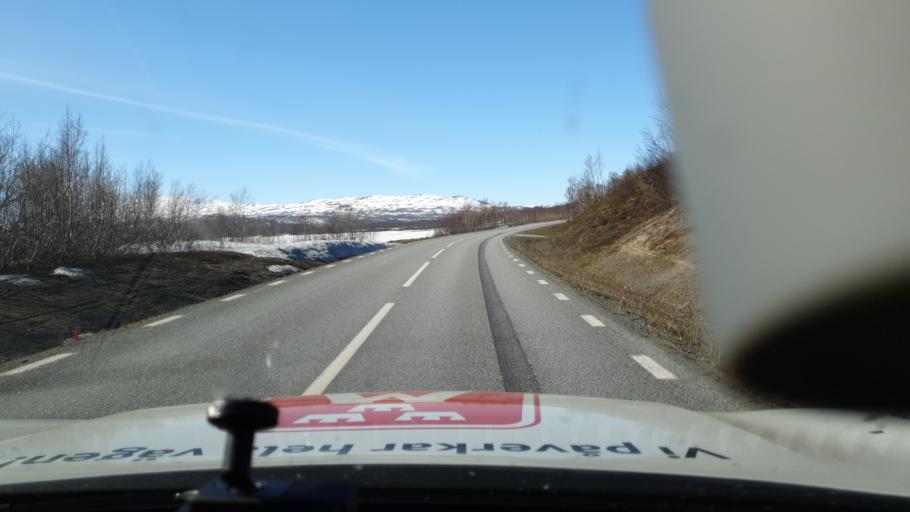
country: NO
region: Nordland
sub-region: Rana
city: Mo i Rana
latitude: 66.0137
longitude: 15.0921
